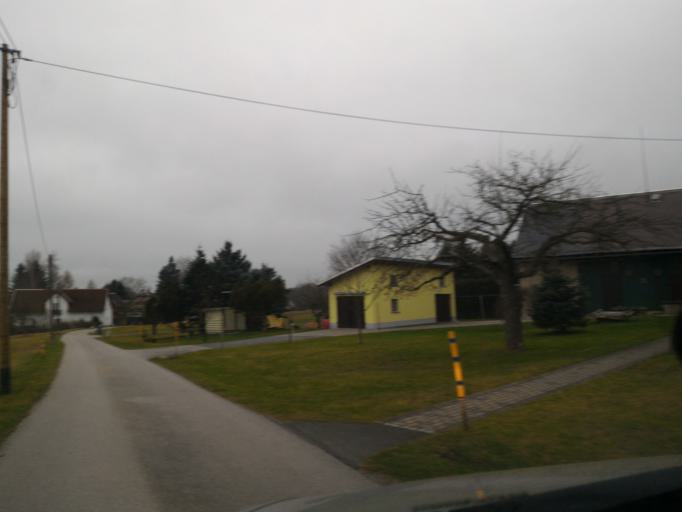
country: DE
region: Saxony
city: Leutersdorf
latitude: 50.9510
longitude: 14.6387
